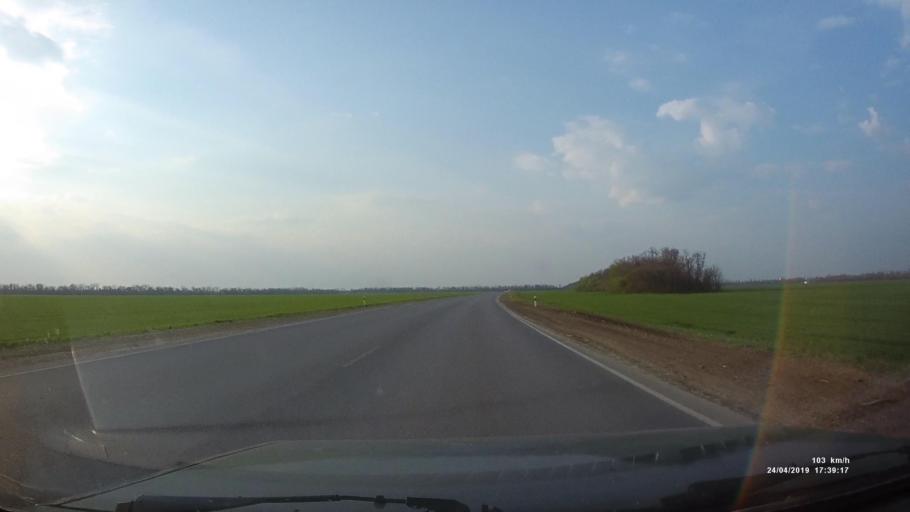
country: RU
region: Rostov
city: Tselina
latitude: 46.5196
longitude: 40.9931
